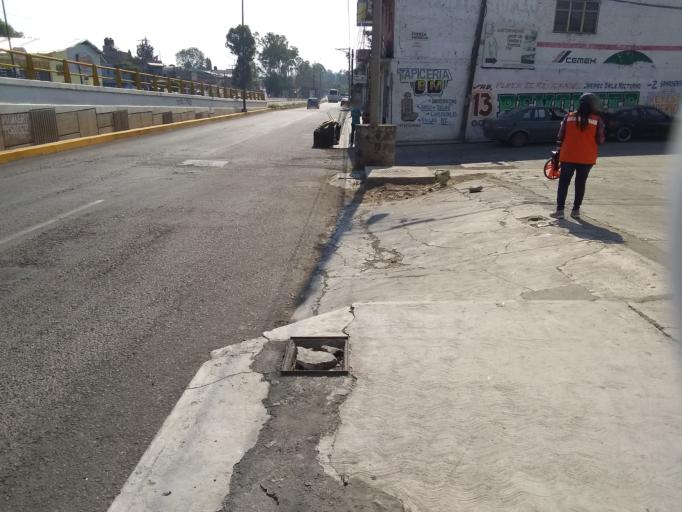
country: MX
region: Michoacan
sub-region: Morelia
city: San Antonio
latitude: 19.7008
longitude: -101.2403
